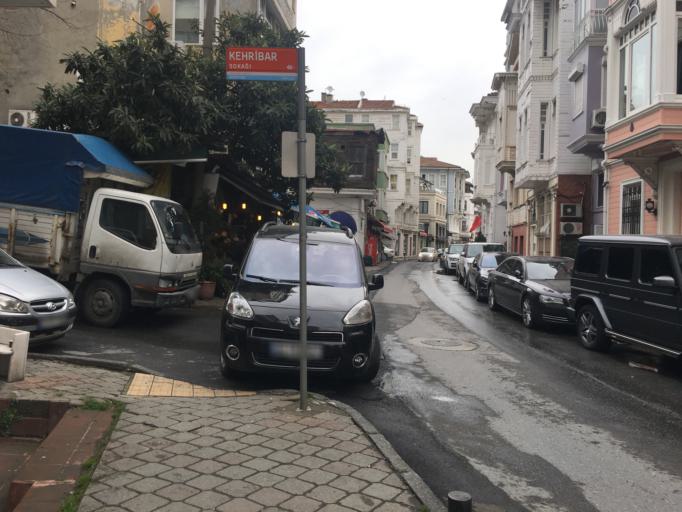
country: TR
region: Istanbul
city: UEskuedar
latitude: 41.0670
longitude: 29.0421
